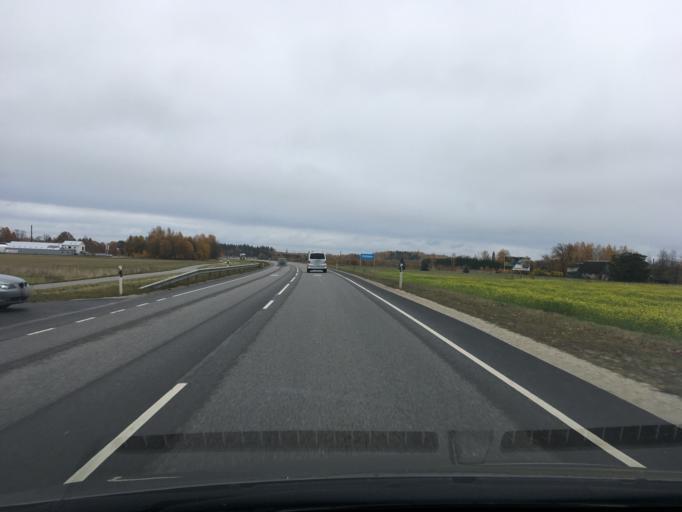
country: EE
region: Tartu
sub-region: UElenurme vald
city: Ulenurme
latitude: 58.3244
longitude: 26.6365
